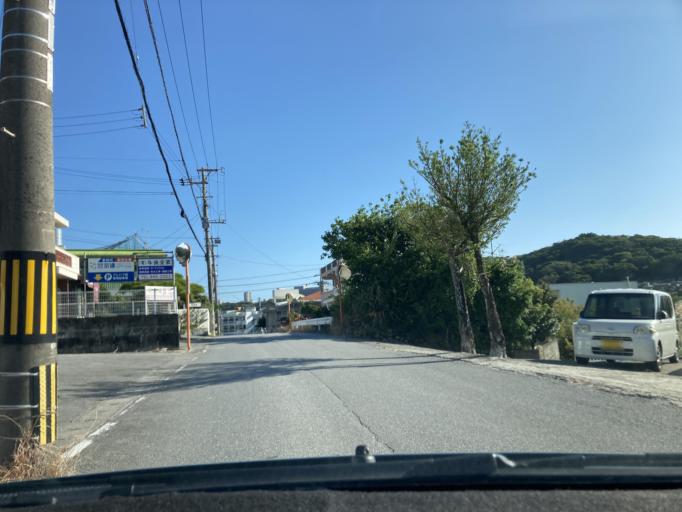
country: JP
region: Okinawa
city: Ginowan
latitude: 26.2512
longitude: 127.7540
